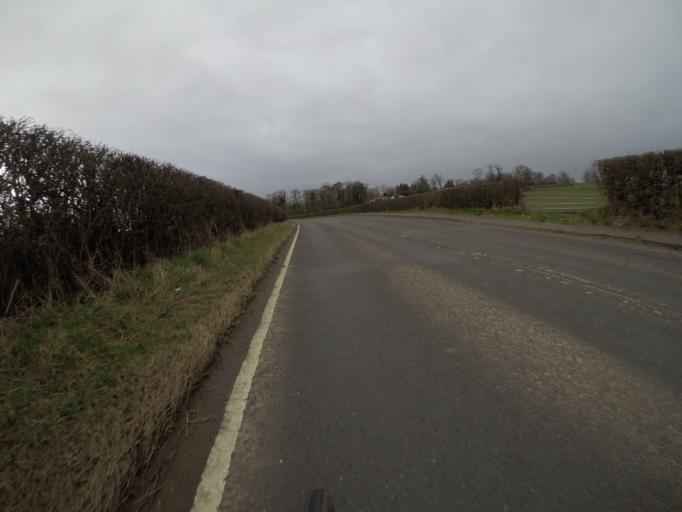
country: GB
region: Scotland
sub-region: East Ayrshire
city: Crosshouse
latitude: 55.6114
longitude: -4.5685
